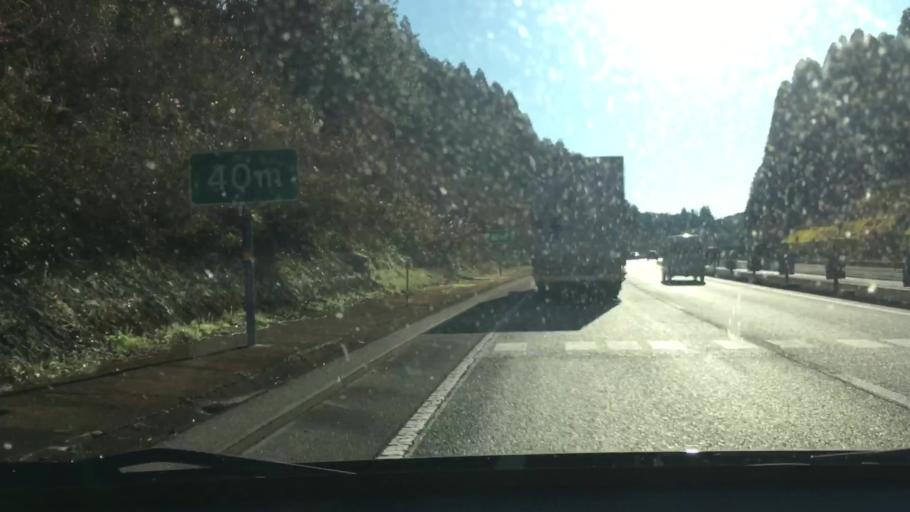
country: JP
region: Kagoshima
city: Kajiki
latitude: 31.8714
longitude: 130.6928
